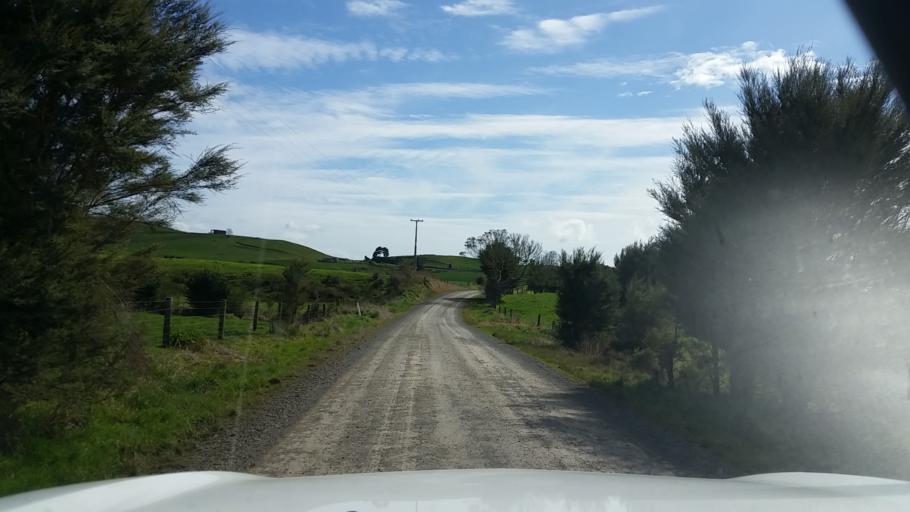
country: NZ
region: Waikato
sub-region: Hauraki District
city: Ngatea
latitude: -37.4513
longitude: 175.4999
